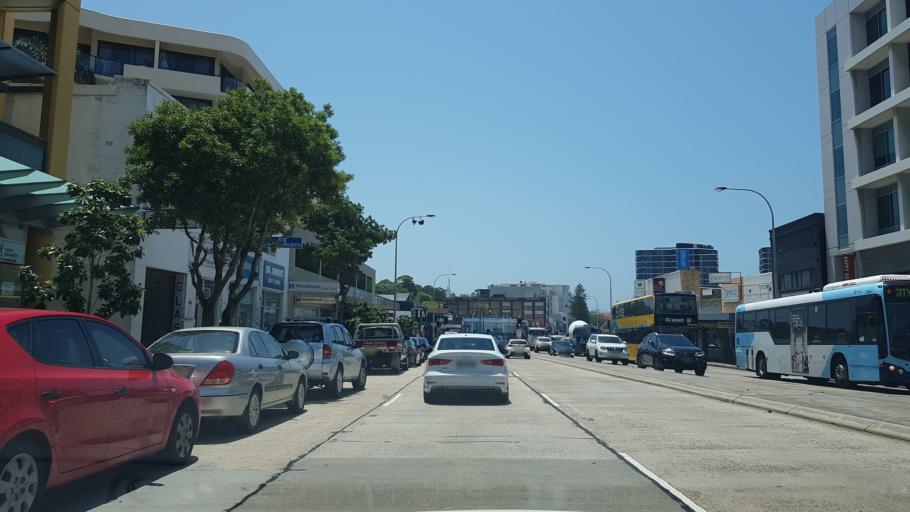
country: AU
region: New South Wales
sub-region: Warringah
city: Narraweena
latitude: -33.7551
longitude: 151.2836
